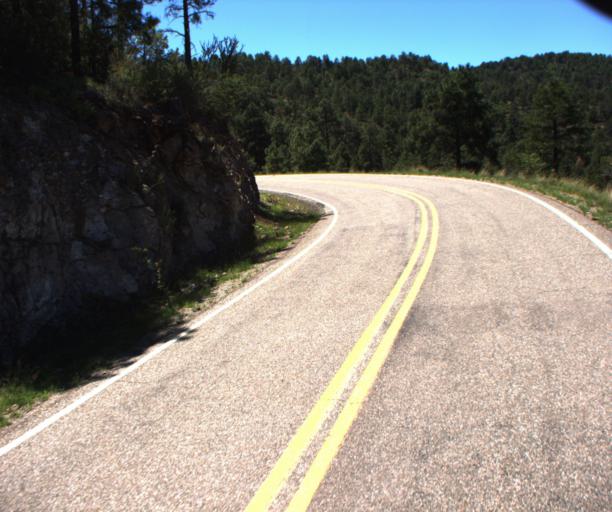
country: US
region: Arizona
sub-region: Greenlee County
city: Morenci
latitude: 33.2408
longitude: -109.3770
